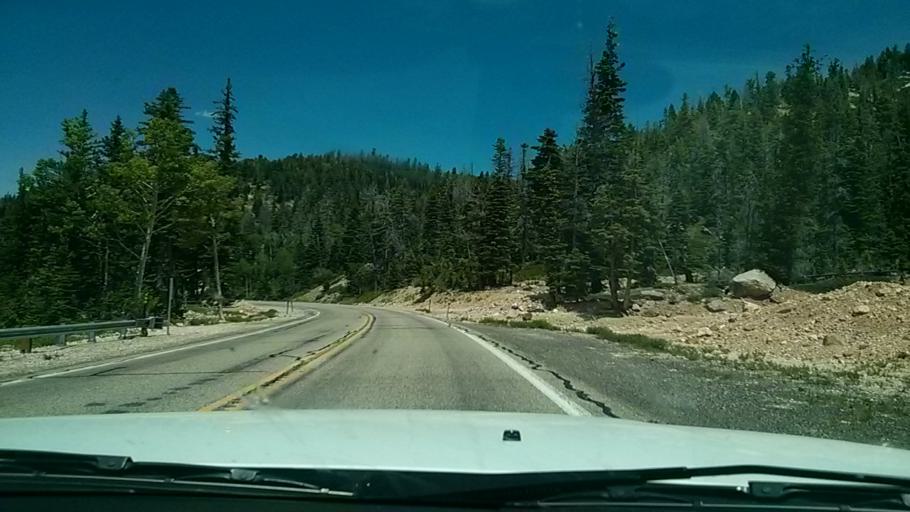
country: US
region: Utah
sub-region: Iron County
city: Cedar City
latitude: 37.5894
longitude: -112.8815
